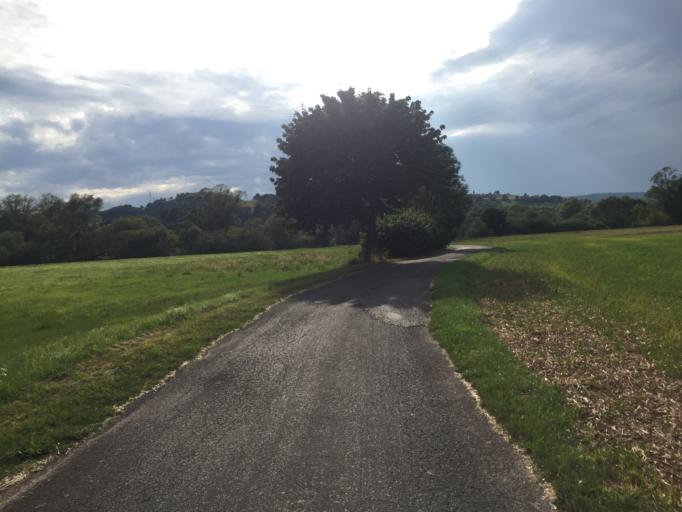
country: DE
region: Hesse
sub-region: Regierungsbezirk Kassel
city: Alheim
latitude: 51.0301
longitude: 9.6771
